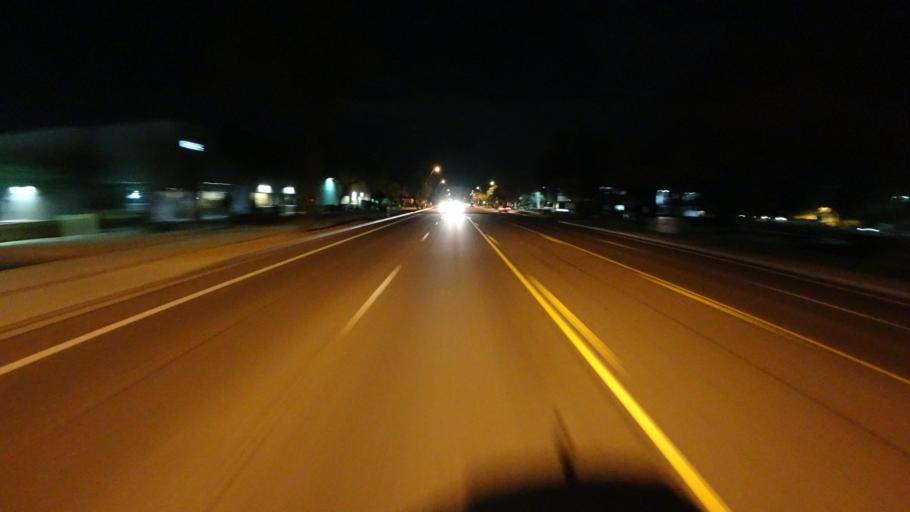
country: US
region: Arizona
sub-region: Maricopa County
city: Guadalupe
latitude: 33.3316
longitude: -111.9457
